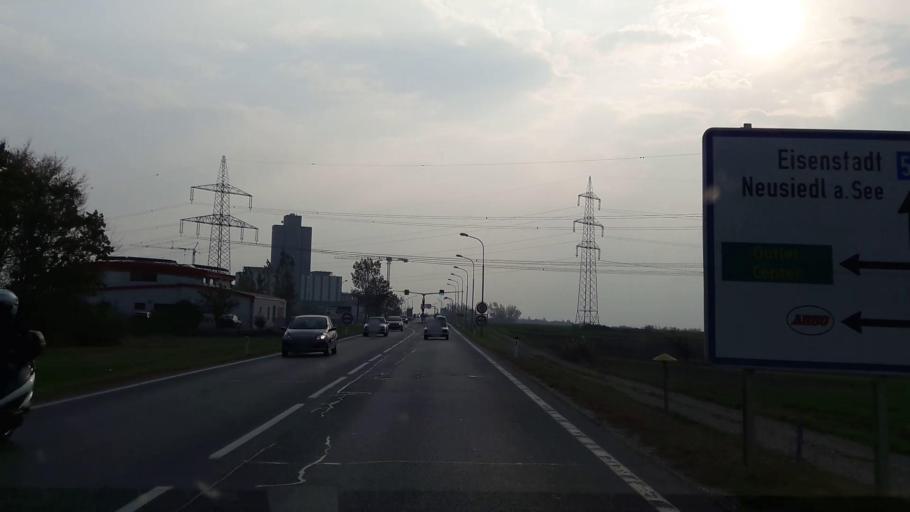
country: AT
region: Burgenland
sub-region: Politischer Bezirk Neusiedl am See
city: Parndorf
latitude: 47.9863
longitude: 16.8524
